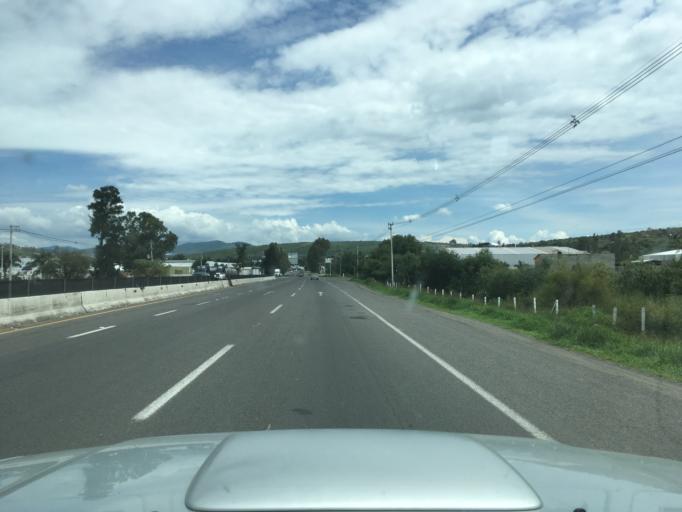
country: MX
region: Michoacan
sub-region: Tarimbaro
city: Conjunto Habitacional el Trebol
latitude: 19.7814
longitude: -101.1578
